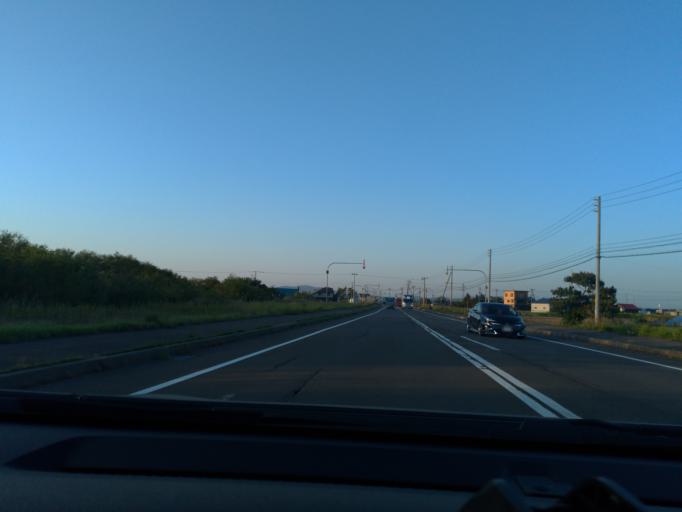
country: JP
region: Hokkaido
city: Tobetsu
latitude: 43.1875
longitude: 141.5242
